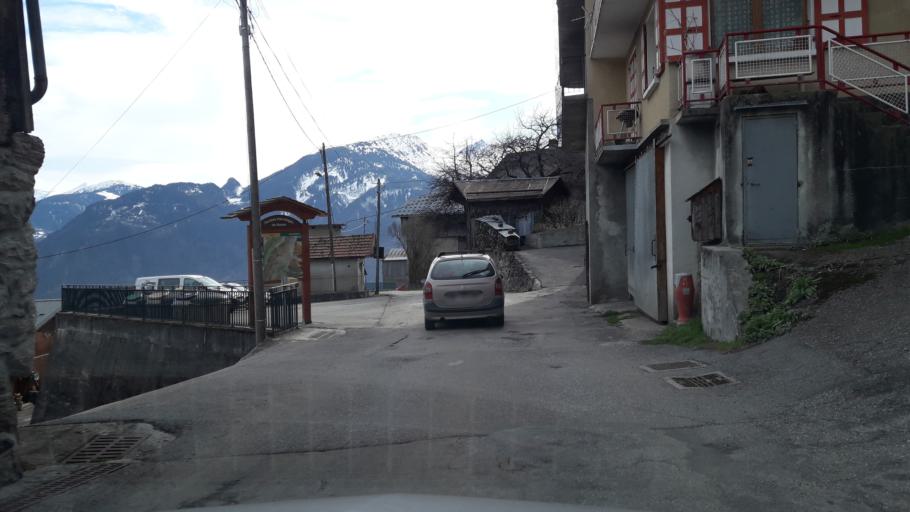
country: FR
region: Rhone-Alpes
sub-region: Departement de la Savoie
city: Aigueblanche
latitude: 45.5402
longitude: 6.4946
